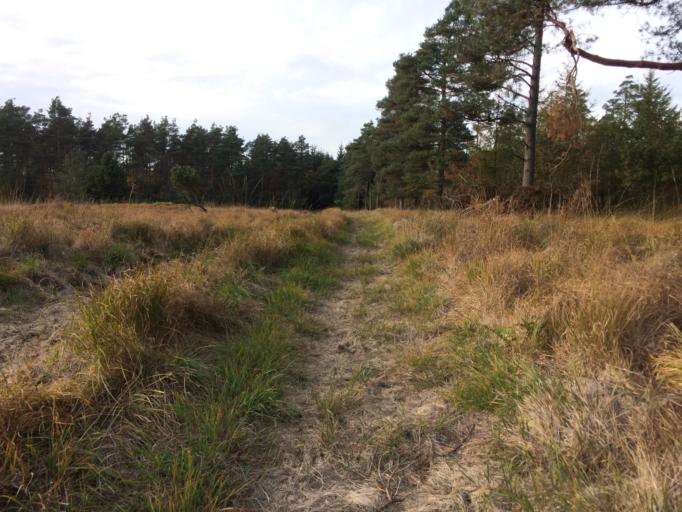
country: DK
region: Central Jutland
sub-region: Holstebro Kommune
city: Ulfborg
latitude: 56.2104
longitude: 8.4689
